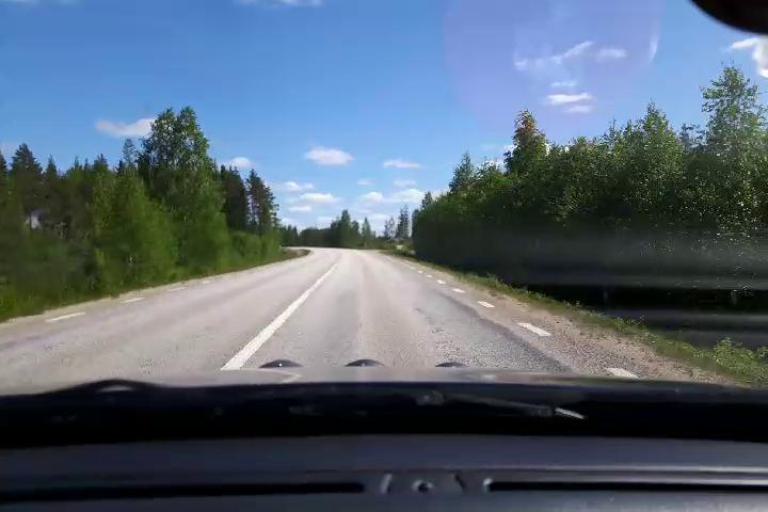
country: SE
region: Gaevleborg
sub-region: Ljusdals Kommun
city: Farila
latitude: 61.9879
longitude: 15.2807
